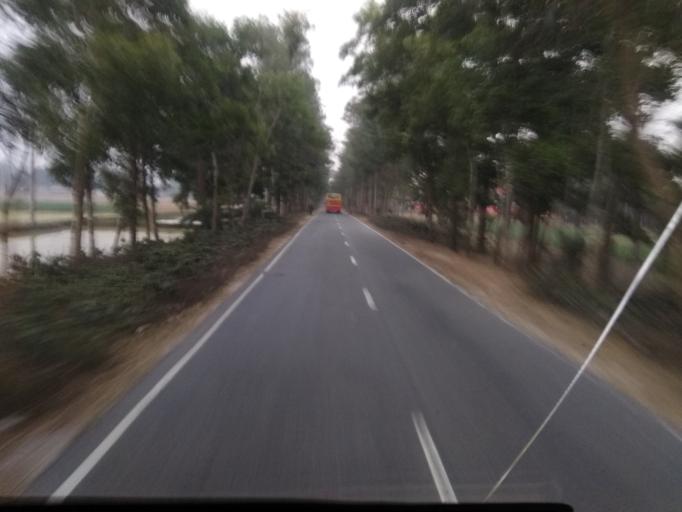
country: BD
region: Rajshahi
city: Bogra
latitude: 24.6892
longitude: 89.2949
